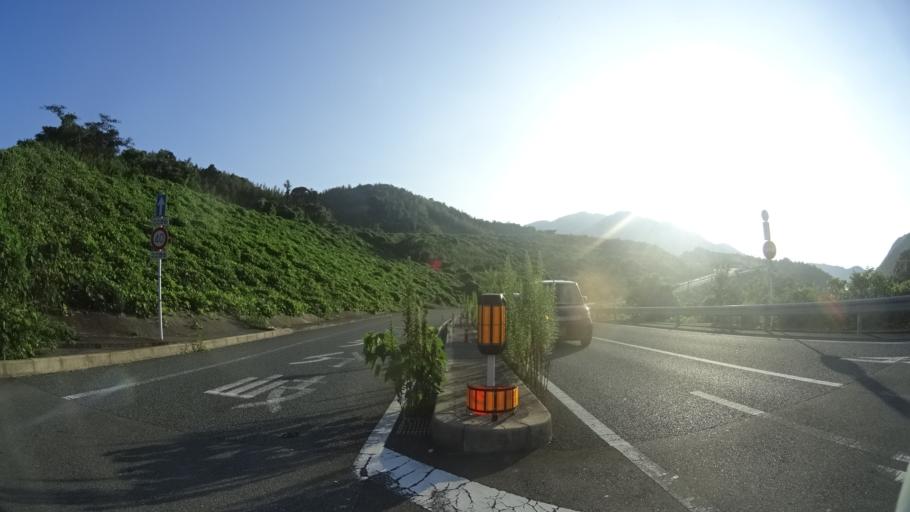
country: JP
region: Yamaguchi
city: Hagi
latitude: 34.3870
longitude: 131.3529
